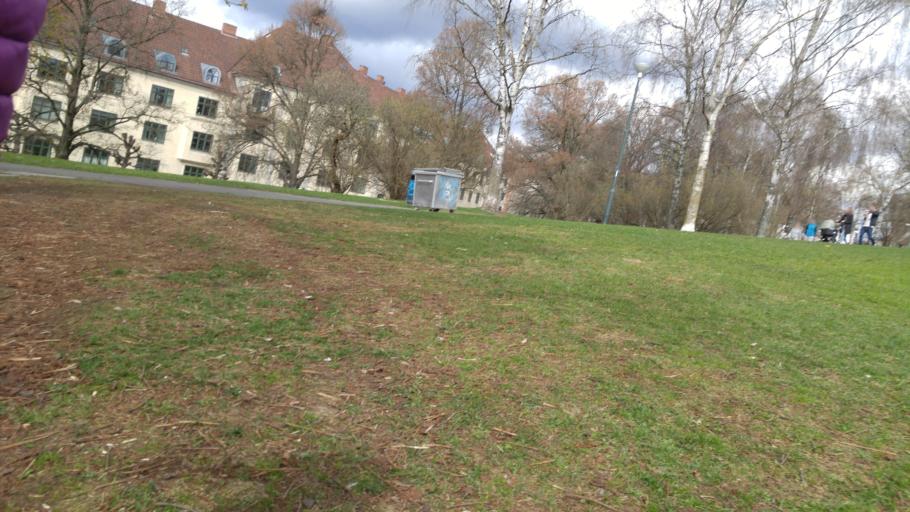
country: NO
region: Oslo
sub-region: Oslo
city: Oslo
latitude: 59.9346
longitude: 10.7695
